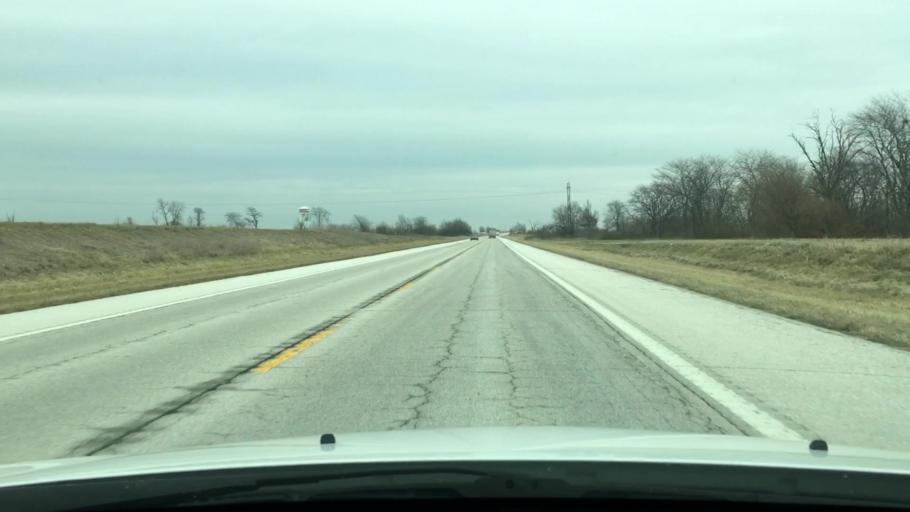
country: US
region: Missouri
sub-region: Pike County
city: Bowling Green
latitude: 39.3481
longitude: -91.2264
